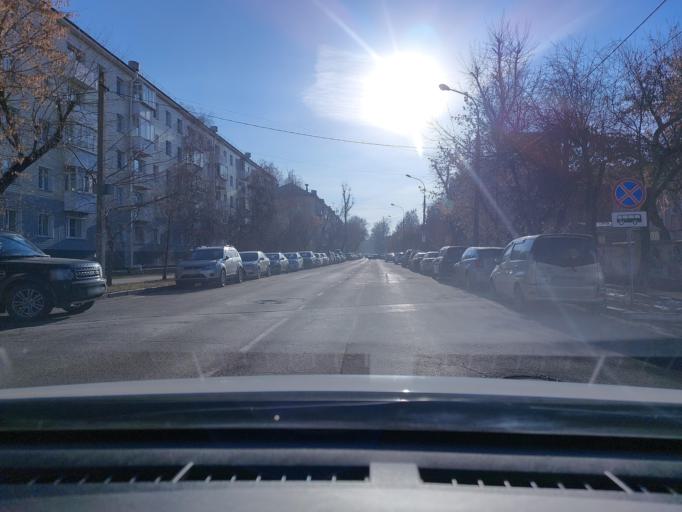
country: RU
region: Irkutsk
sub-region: Irkutskiy Rayon
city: Irkutsk
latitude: 52.2881
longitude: 104.2758
